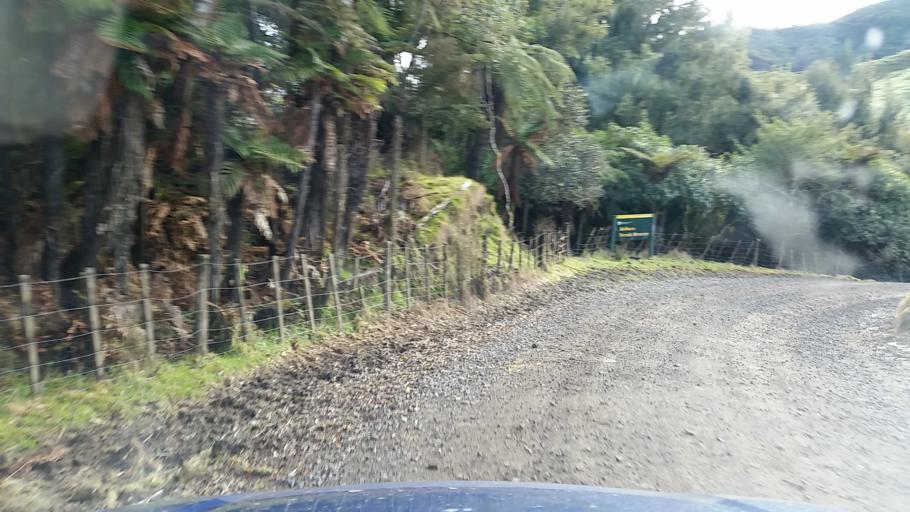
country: NZ
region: Taranaki
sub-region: New Plymouth District
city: Waitara
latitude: -39.1059
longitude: 174.8459
